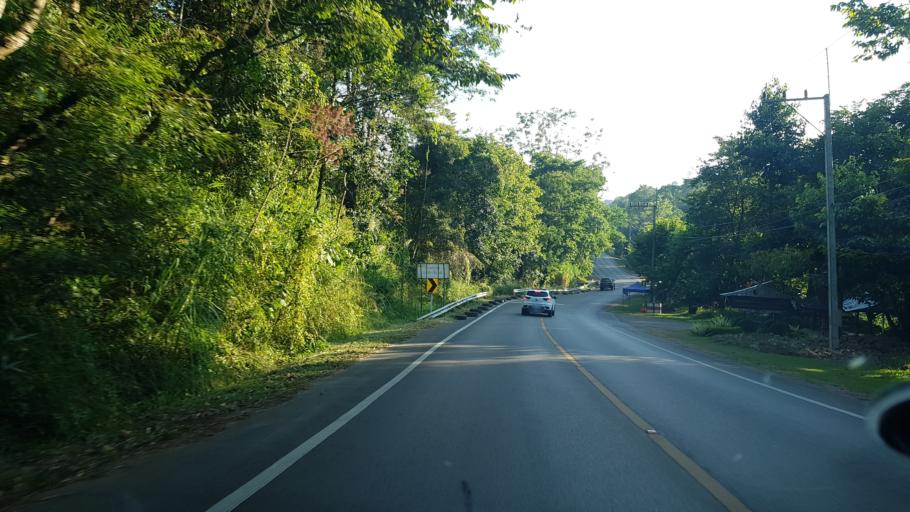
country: TH
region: Chiang Rai
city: Mae Fa Luang
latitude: 20.3026
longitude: 99.8163
